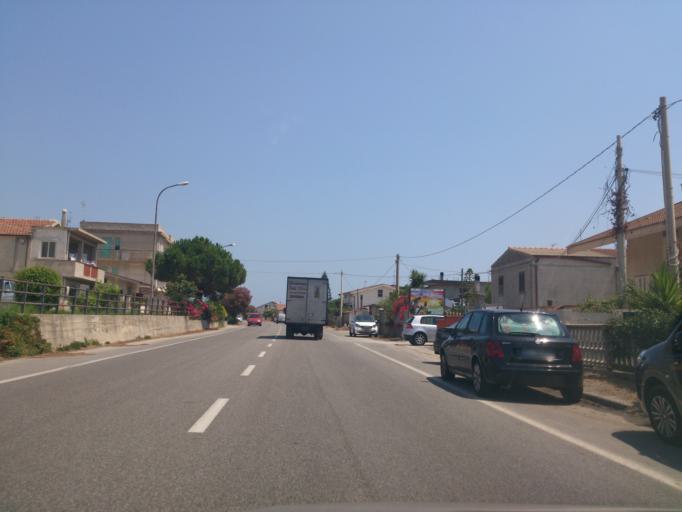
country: IT
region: Calabria
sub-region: Provincia di Reggio Calabria
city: Riace Marina
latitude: 38.3995
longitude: 16.5411
